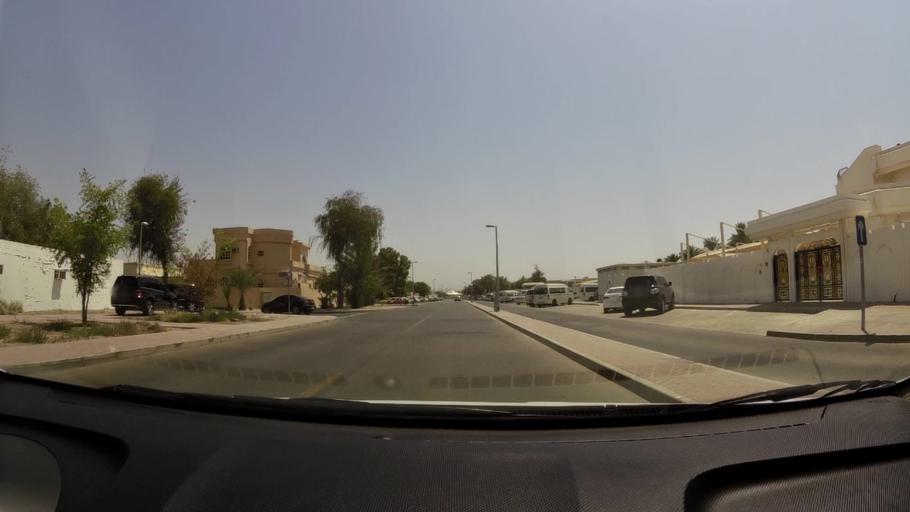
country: AE
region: Ash Shariqah
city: Sharjah
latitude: 25.2859
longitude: 55.3465
